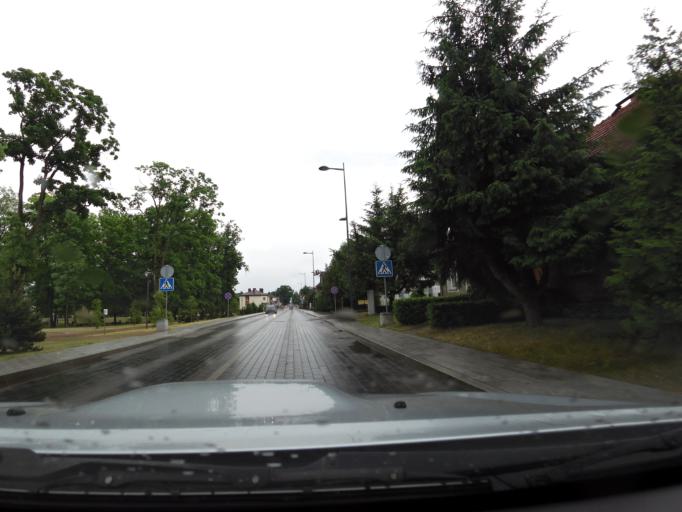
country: LT
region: Marijampoles apskritis
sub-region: Marijampole Municipality
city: Marijampole
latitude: 54.5531
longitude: 23.3448
